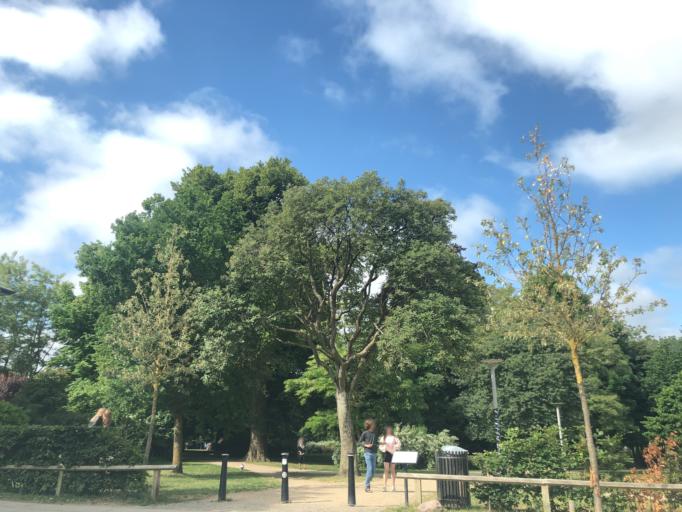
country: DK
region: Zealand
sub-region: Koge Kommune
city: Koge
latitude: 55.4598
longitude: 12.1812
